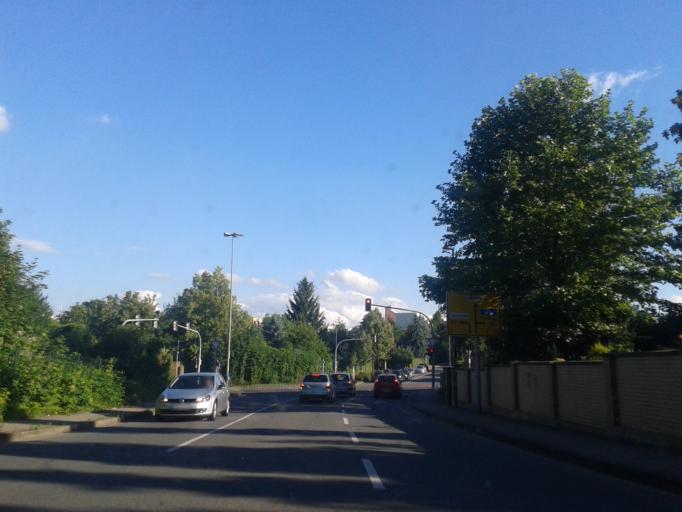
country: DE
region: Saxony
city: Freital
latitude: 51.0509
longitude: 13.6723
